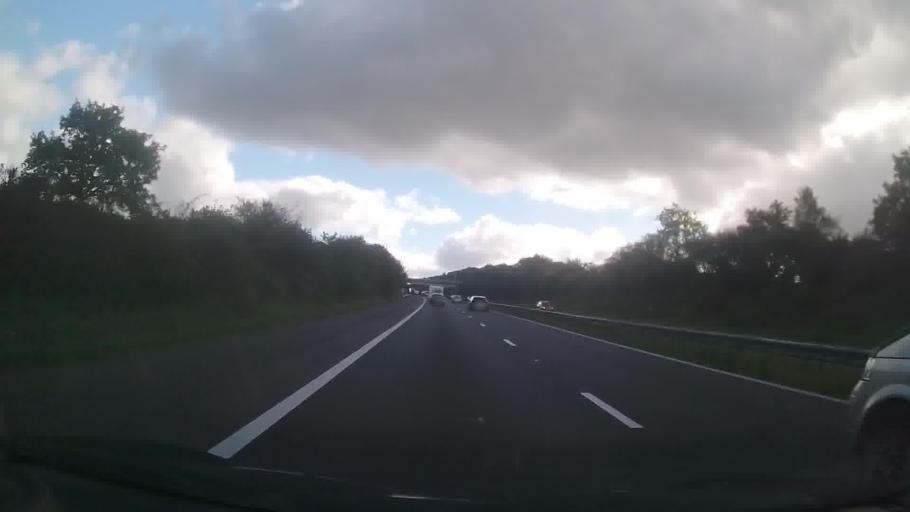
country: GB
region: Wales
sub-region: City and County of Swansea
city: Pontlliw
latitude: 51.6785
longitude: -4.0092
